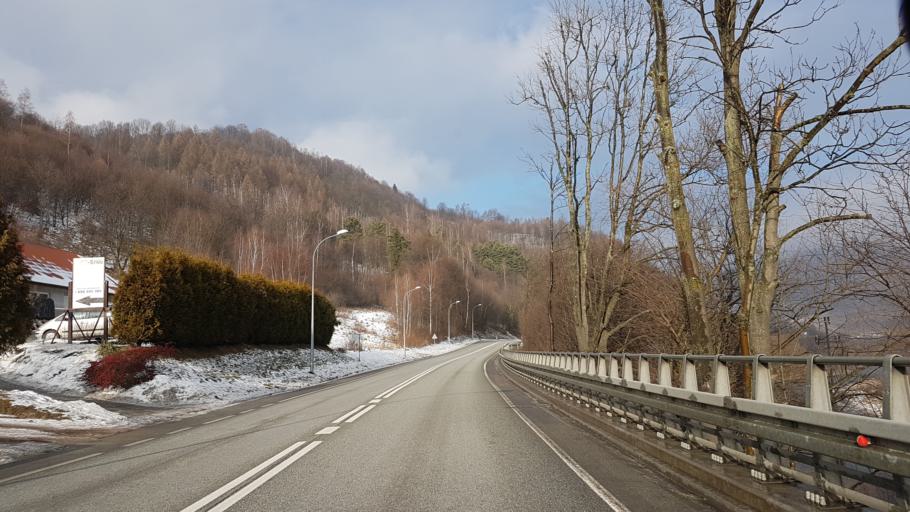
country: PL
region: Lesser Poland Voivodeship
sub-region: Powiat nowosadecki
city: Piwniczna-Zdroj
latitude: 49.4568
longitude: 20.6944
